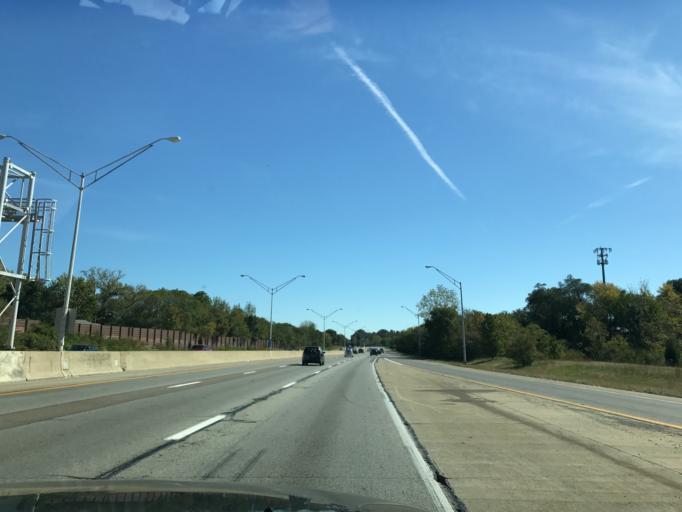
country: US
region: Ohio
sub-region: Franklin County
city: Bexley
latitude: 39.9806
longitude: -82.9518
